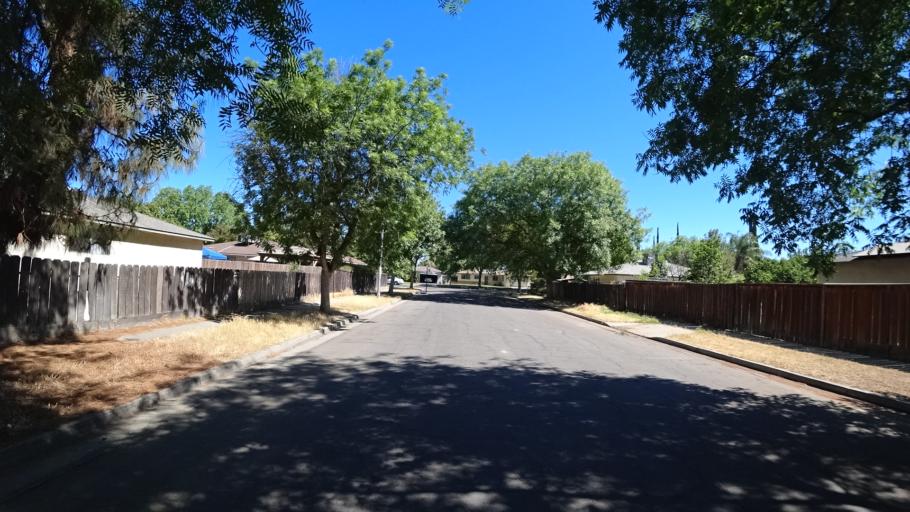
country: US
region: California
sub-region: Fresno County
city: Fresno
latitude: 36.8051
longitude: -119.8467
